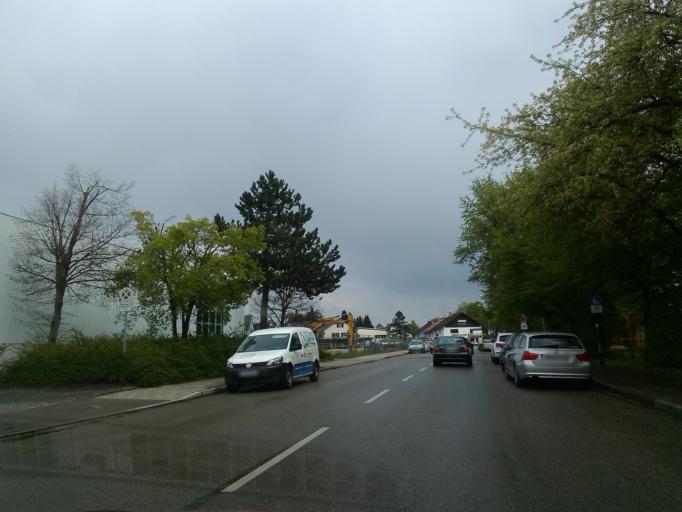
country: DE
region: Bavaria
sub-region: Upper Bavaria
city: Grafelfing
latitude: 48.1095
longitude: 11.4498
